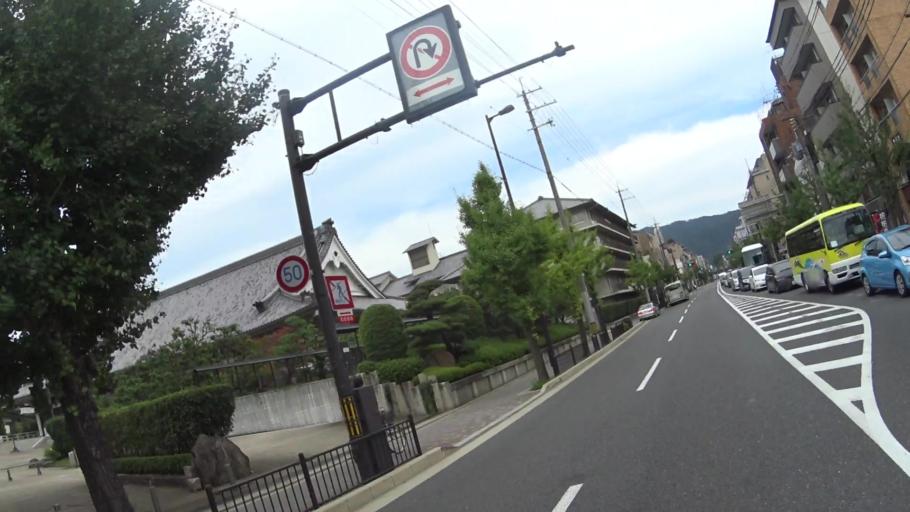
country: JP
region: Kyoto
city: Kyoto
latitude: 35.0176
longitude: 135.7727
